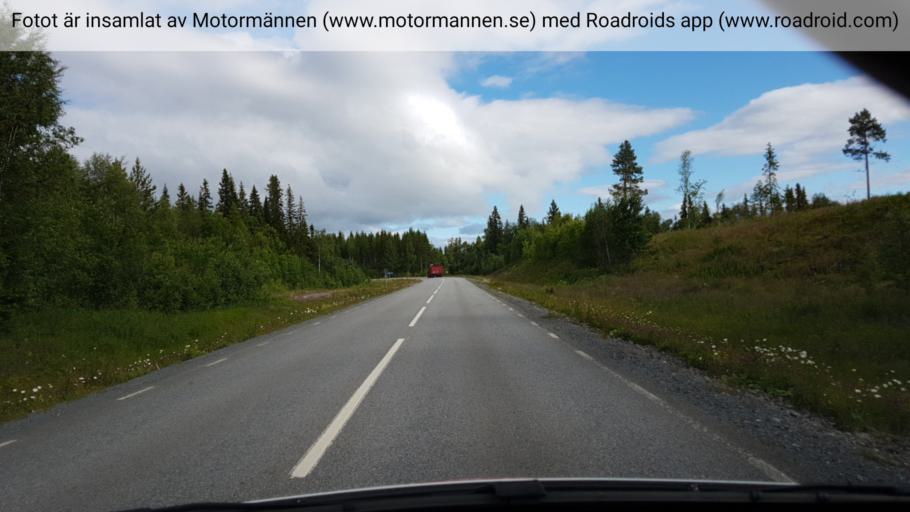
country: SE
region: Jaemtland
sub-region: Krokoms Kommun
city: Krokom
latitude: 63.2856
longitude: 14.4425
